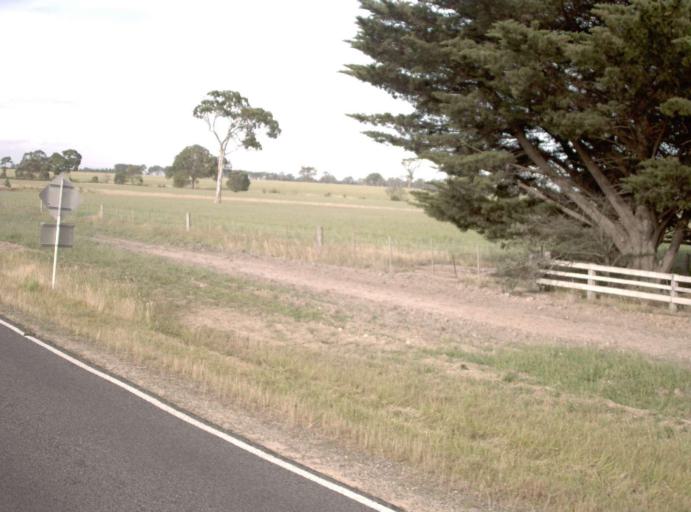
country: AU
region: Victoria
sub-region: Wellington
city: Heyfield
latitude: -38.0557
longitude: 146.6628
